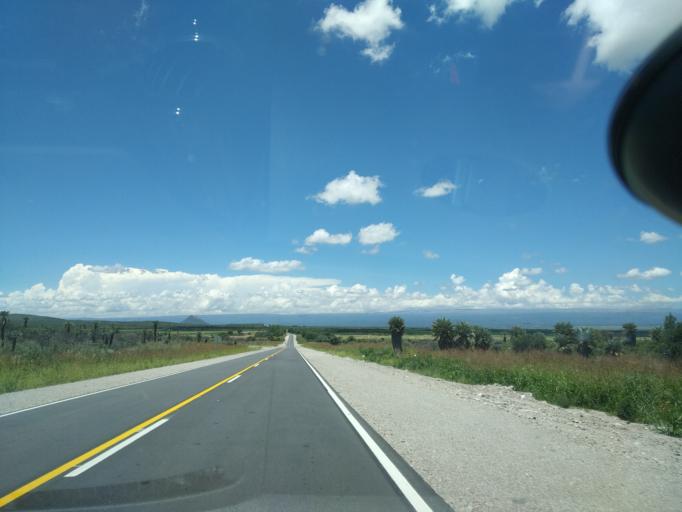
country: AR
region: Cordoba
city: Salsacate
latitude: -31.3735
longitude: -65.2719
